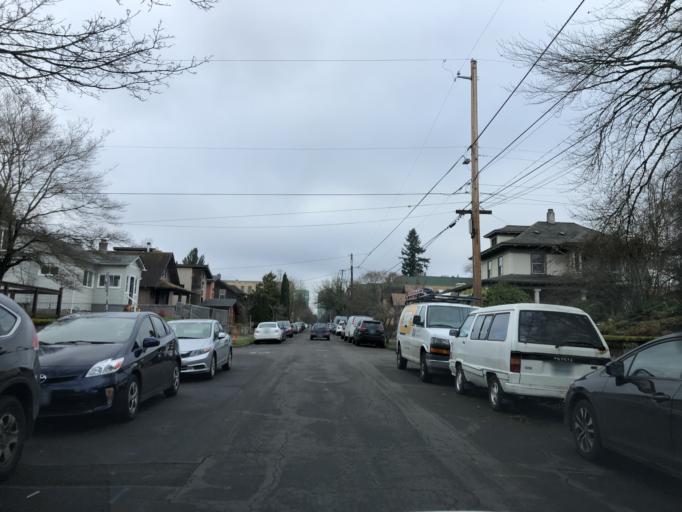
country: US
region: Oregon
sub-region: Multnomah County
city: Portland
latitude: 45.5607
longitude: -122.6458
